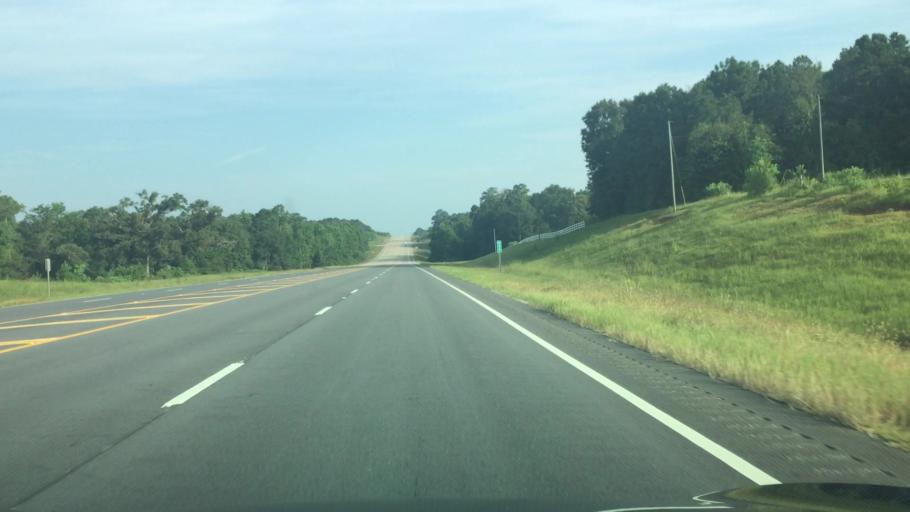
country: US
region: Alabama
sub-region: Butler County
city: Georgiana
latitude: 31.5323
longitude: -86.7222
